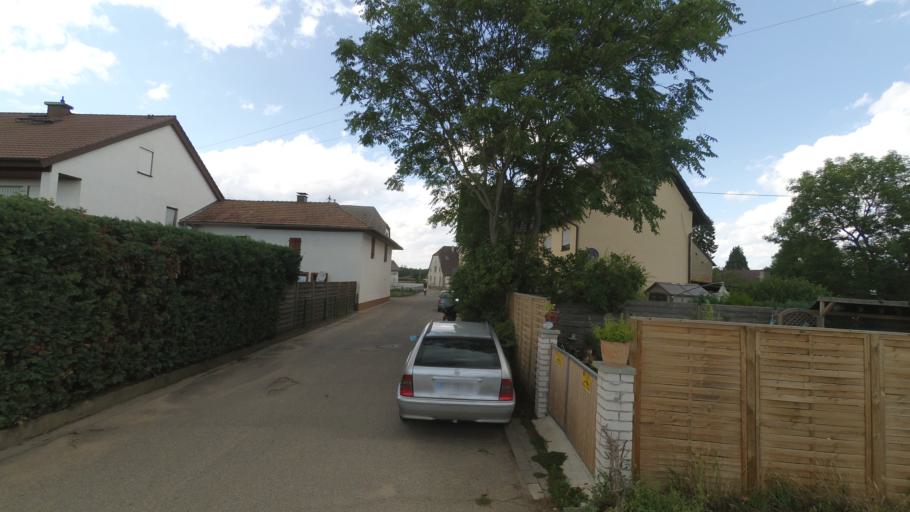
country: DE
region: Rheinland-Pfalz
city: Limburgerhof
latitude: 49.4039
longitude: 8.3978
